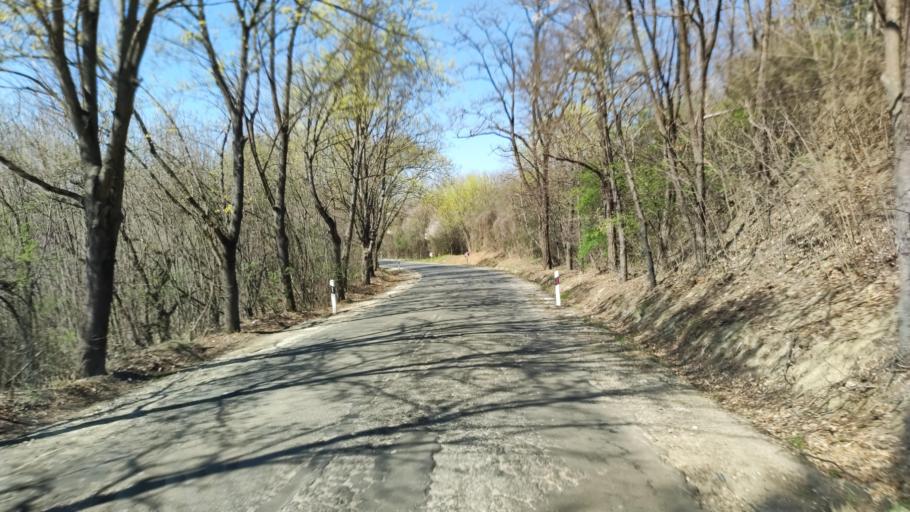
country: HU
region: Pest
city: Kosd
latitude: 47.7957
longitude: 19.1701
